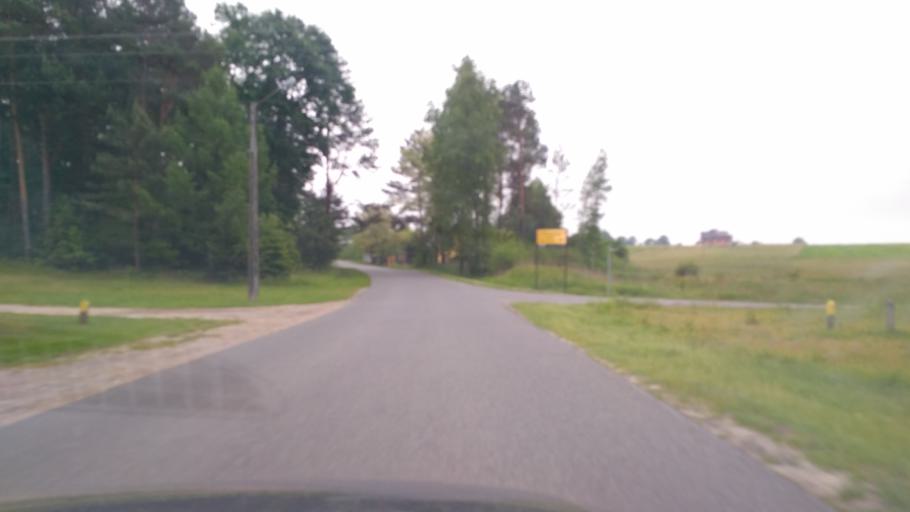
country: PL
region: Subcarpathian Voivodeship
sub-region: Powiat kolbuszowski
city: Niwiska
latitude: 50.1749
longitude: 21.6643
